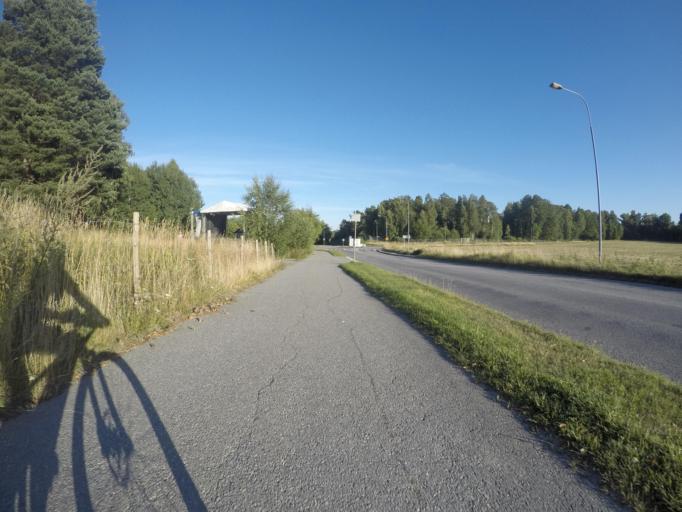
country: SE
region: Vaestmanland
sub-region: Vasteras
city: Vasteras
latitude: 59.5859
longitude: 16.6214
